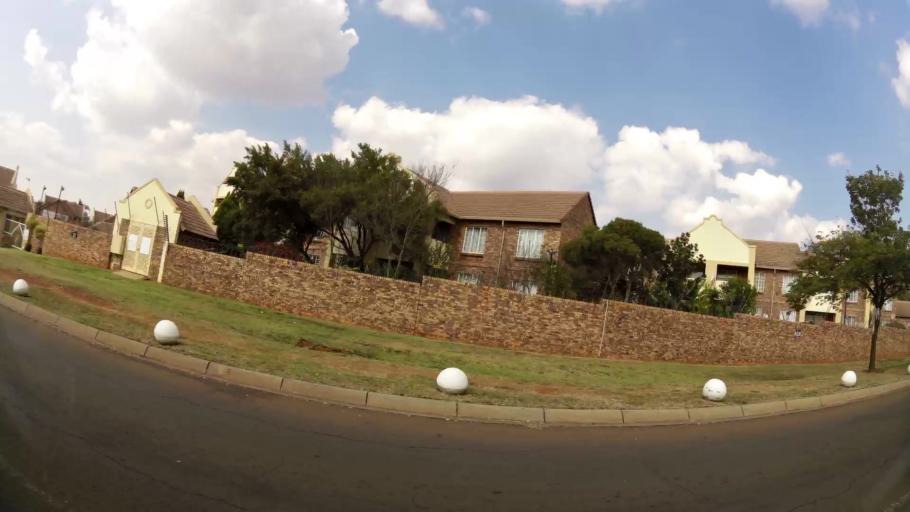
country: ZA
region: Gauteng
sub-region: City of Tshwane Metropolitan Municipality
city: Pretoria
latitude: -25.8017
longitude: 28.3234
